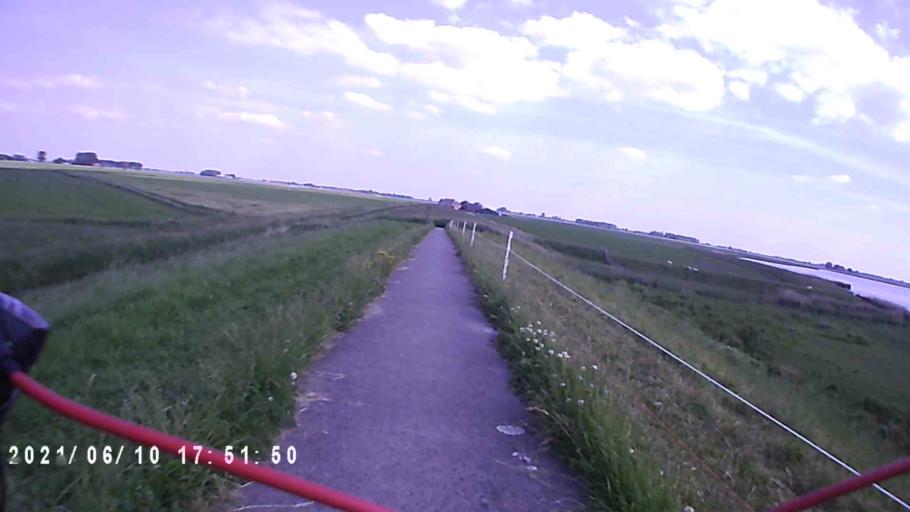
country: NL
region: Groningen
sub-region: Gemeente De Marne
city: Ulrum
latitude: 53.3301
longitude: 6.3147
